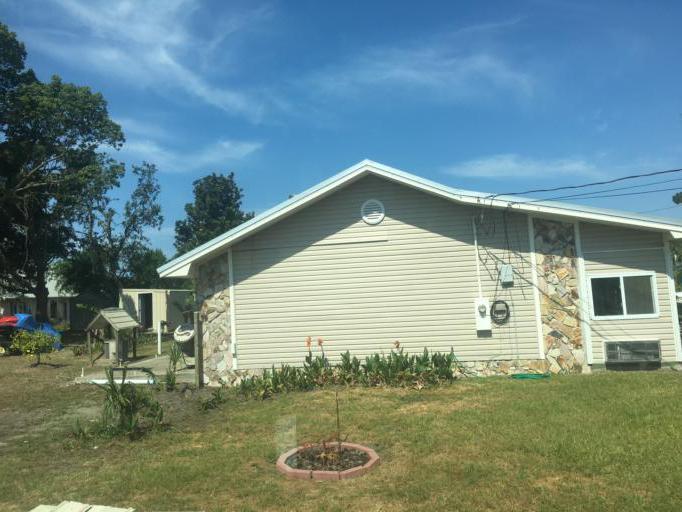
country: US
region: Florida
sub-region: Bay County
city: Upper Grand Lagoon
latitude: 30.1645
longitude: -85.7633
